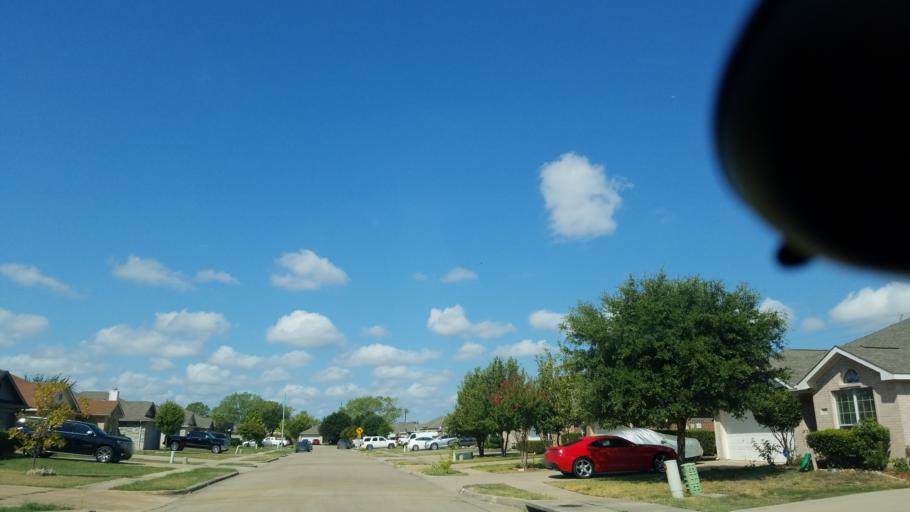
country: US
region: Texas
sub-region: Dallas County
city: Grand Prairie
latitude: 32.7100
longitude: -96.9892
